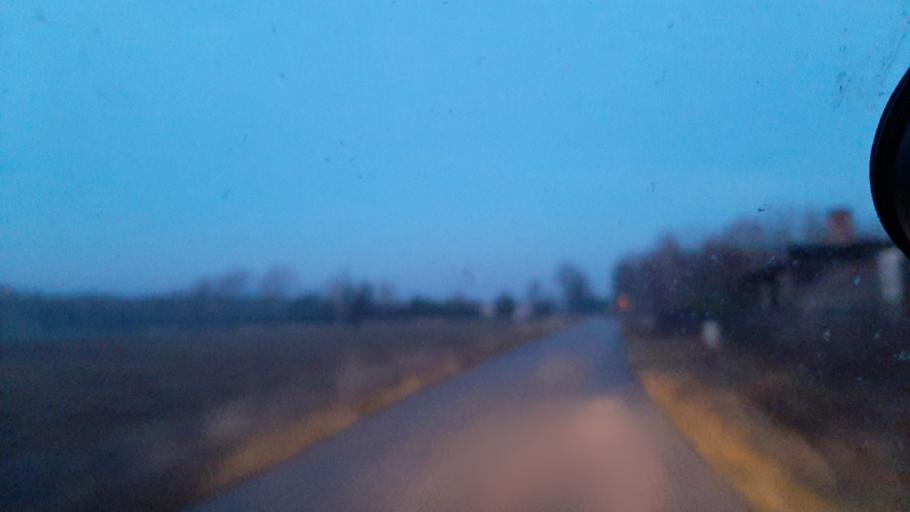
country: PL
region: Lublin Voivodeship
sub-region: Powiat lubartowski
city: Firlej
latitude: 51.5280
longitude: 22.4993
